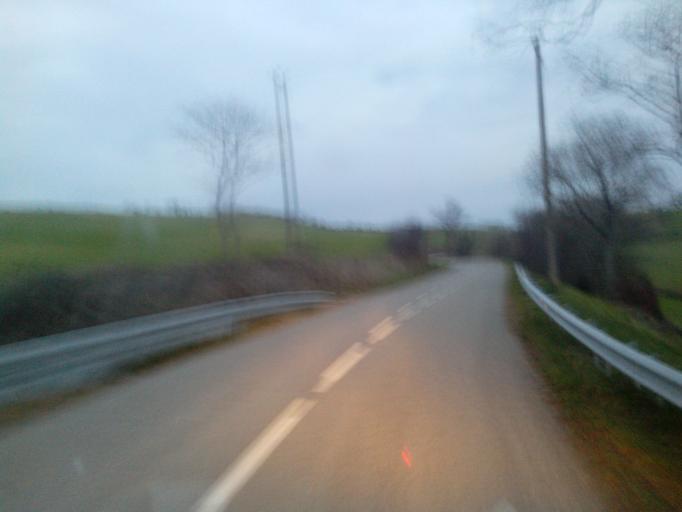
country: FR
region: Languedoc-Roussillon
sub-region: Departement de l'Aude
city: Belpech
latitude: 43.2726
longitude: 1.7648
